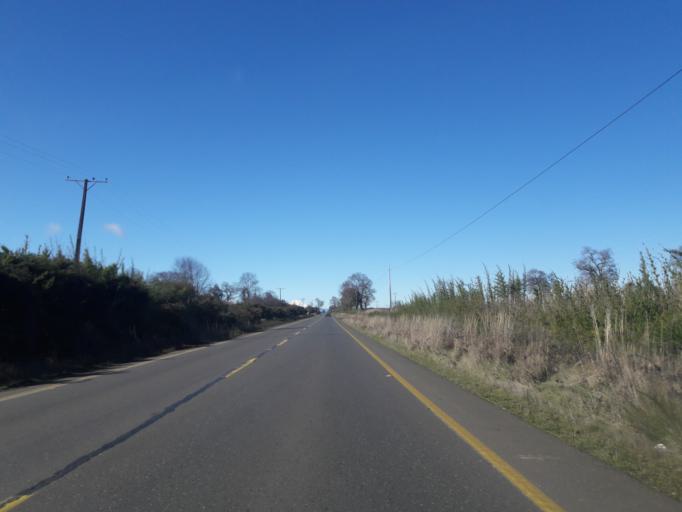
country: CL
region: Araucania
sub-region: Provincia de Malleco
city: Victoria
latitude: -38.2598
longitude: -72.2542
